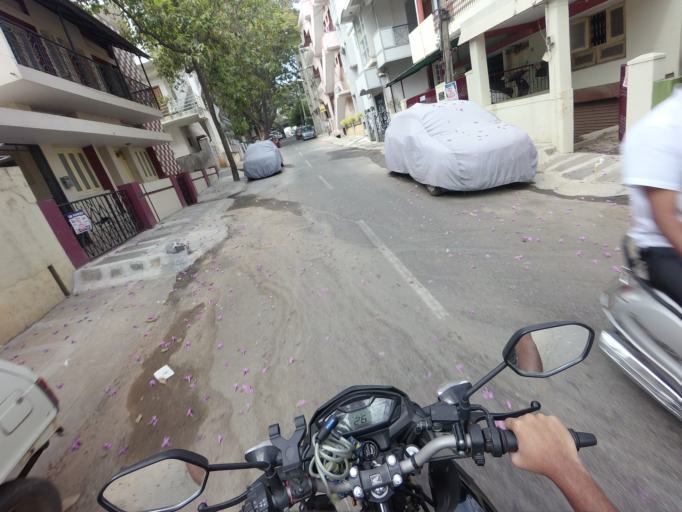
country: IN
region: Karnataka
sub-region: Bangalore Urban
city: Bangalore
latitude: 12.9703
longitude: 77.5387
